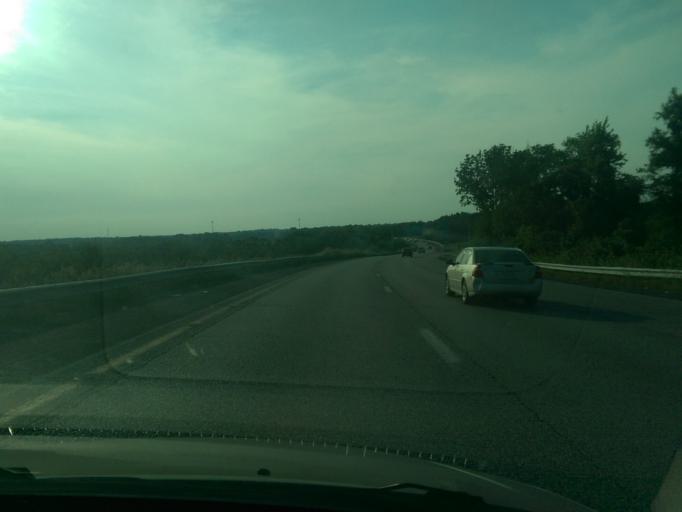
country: US
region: Missouri
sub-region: Platte County
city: Riverside
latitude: 39.1810
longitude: -94.5868
